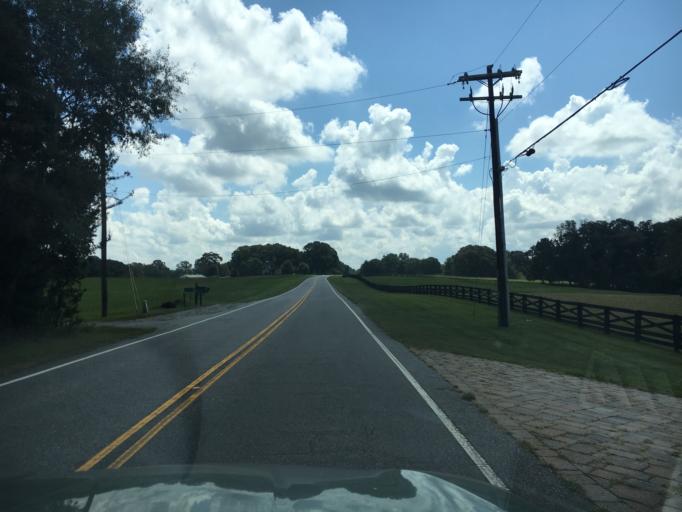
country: US
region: South Carolina
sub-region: Spartanburg County
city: Fairforest
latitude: 34.9052
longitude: -82.0429
